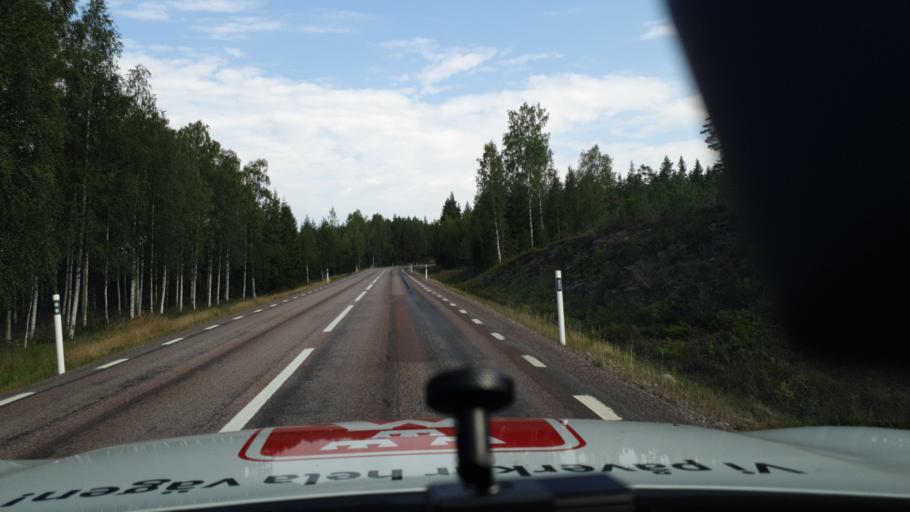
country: SE
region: Vaermland
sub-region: Hagfors Kommun
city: Ekshaerad
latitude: 60.4754
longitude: 13.3059
